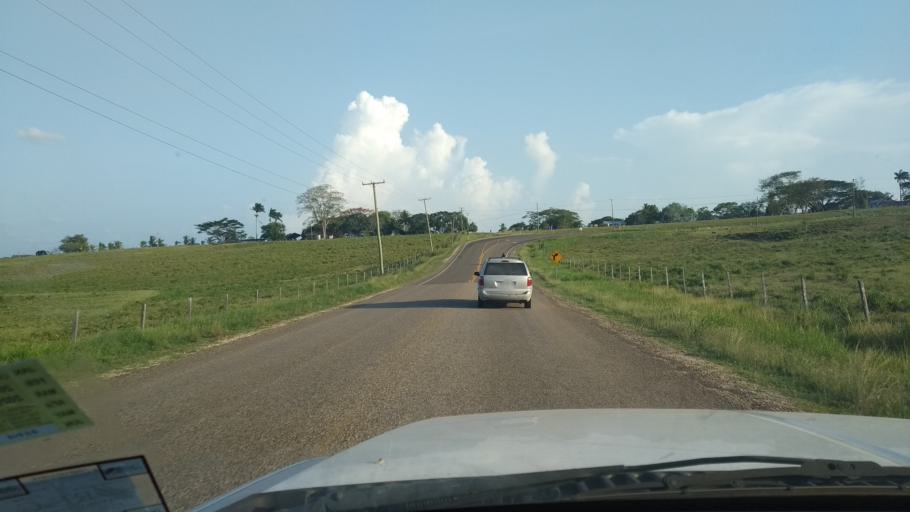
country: BZ
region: Cayo
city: San Ignacio
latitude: 17.2464
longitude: -88.9874
